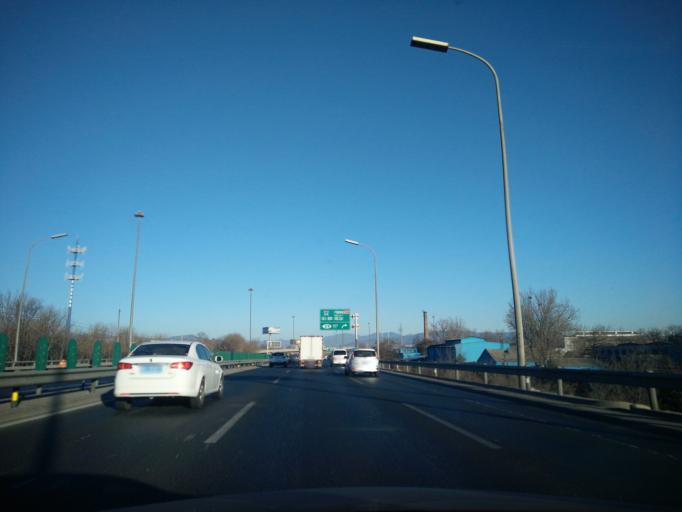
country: CN
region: Beijing
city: Fengtai
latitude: 39.8399
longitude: 116.2233
